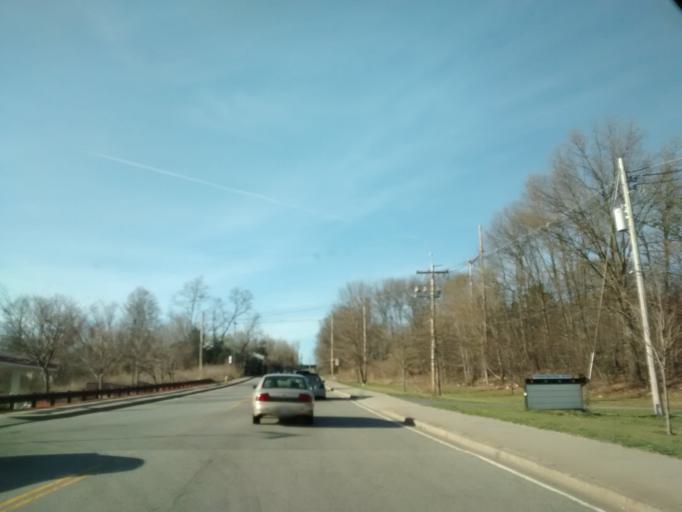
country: US
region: Massachusetts
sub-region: Worcester County
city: Sunderland
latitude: 42.2372
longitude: -71.7922
